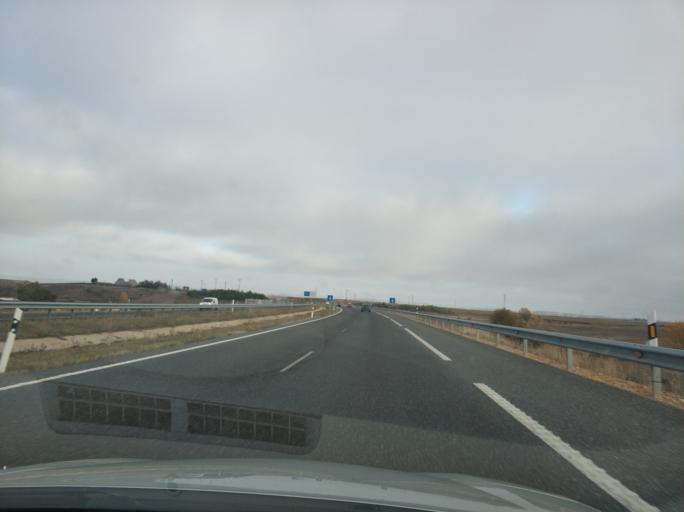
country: ES
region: Castille and Leon
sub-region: Provincia de Leon
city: Valdefresno
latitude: 42.5617
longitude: -5.5010
